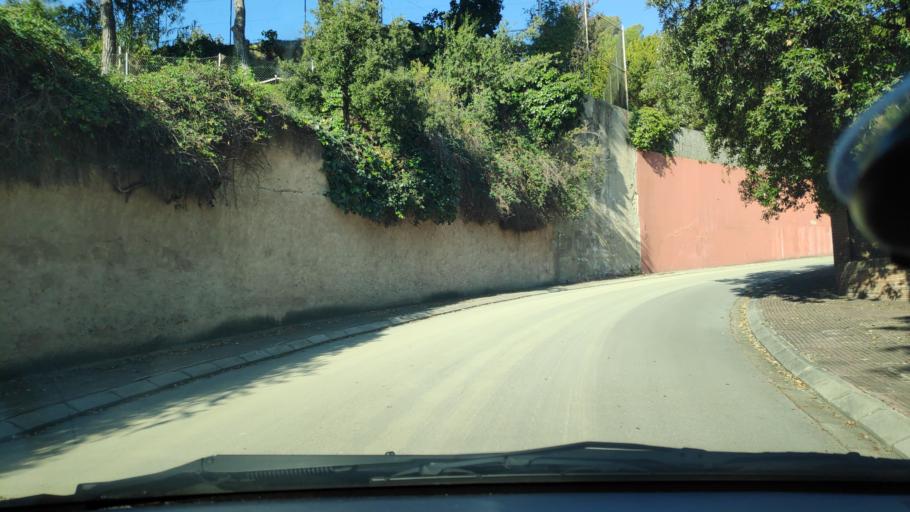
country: ES
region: Catalonia
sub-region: Provincia de Barcelona
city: Sant Quirze del Valles
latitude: 41.5073
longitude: 2.0817
